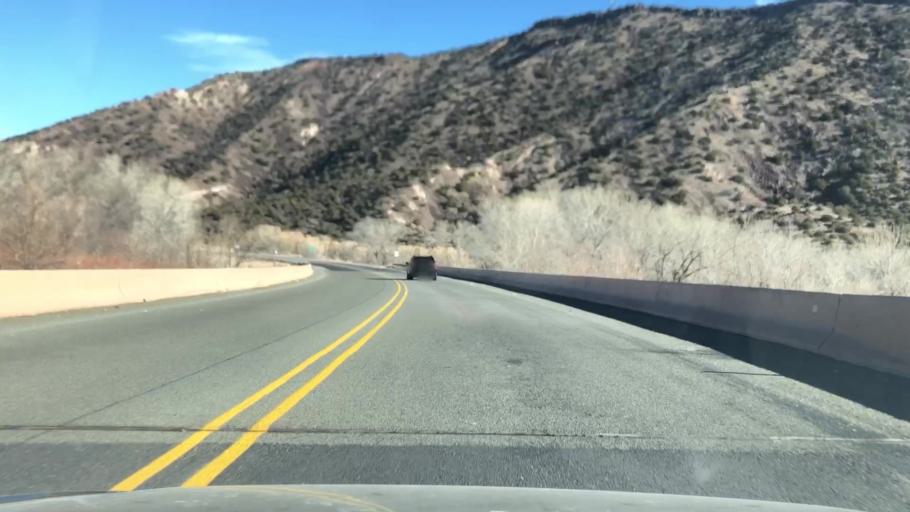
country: US
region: New Mexico
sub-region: Rio Arriba County
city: Ohkay Owingeh
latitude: 36.0942
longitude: -106.1320
